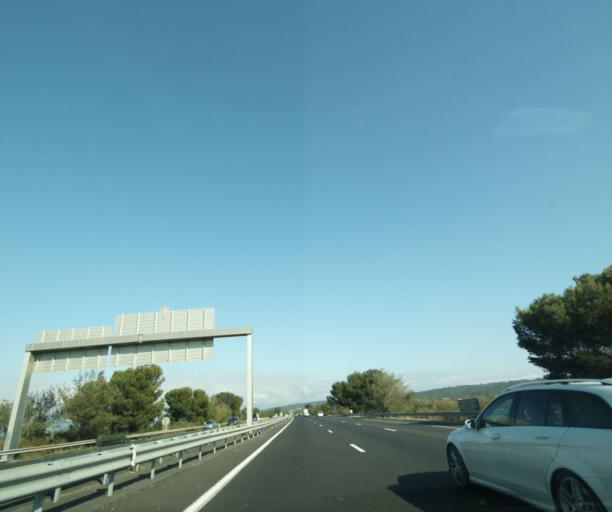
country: FR
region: Languedoc-Roussillon
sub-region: Departement de l'Aude
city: Narbonne
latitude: 43.1779
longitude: 3.0379
